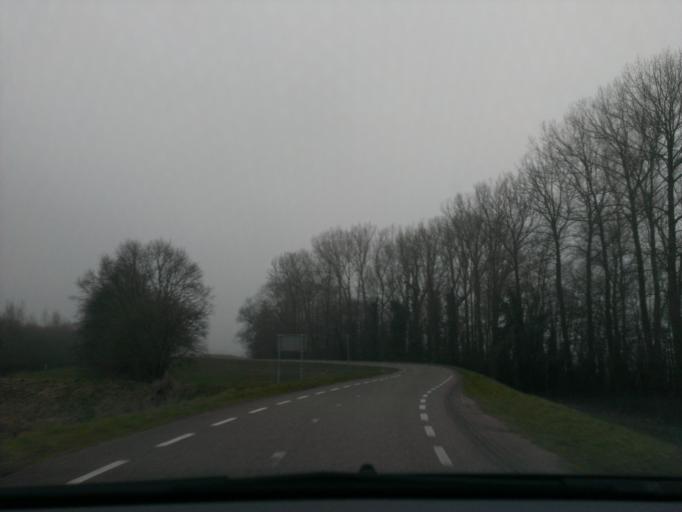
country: NL
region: Overijssel
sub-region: Gemeente Olst-Wijhe
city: Olst
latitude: 52.3004
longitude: 6.0937
